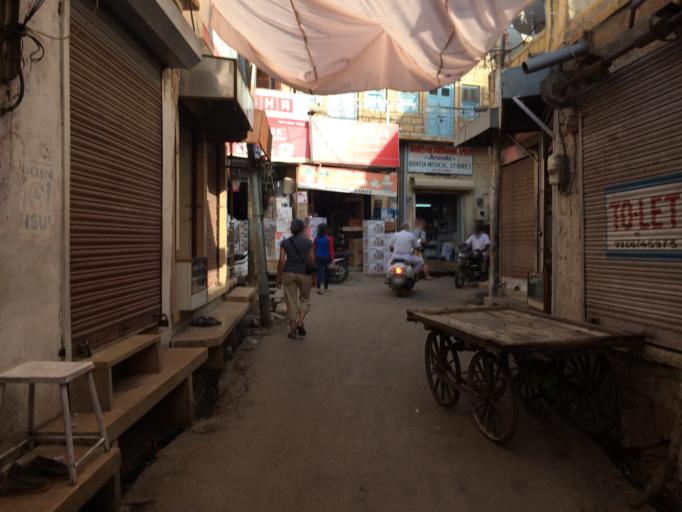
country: IN
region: Rajasthan
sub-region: Jaisalmer
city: Jaisalmer
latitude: 26.9154
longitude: 70.9124
